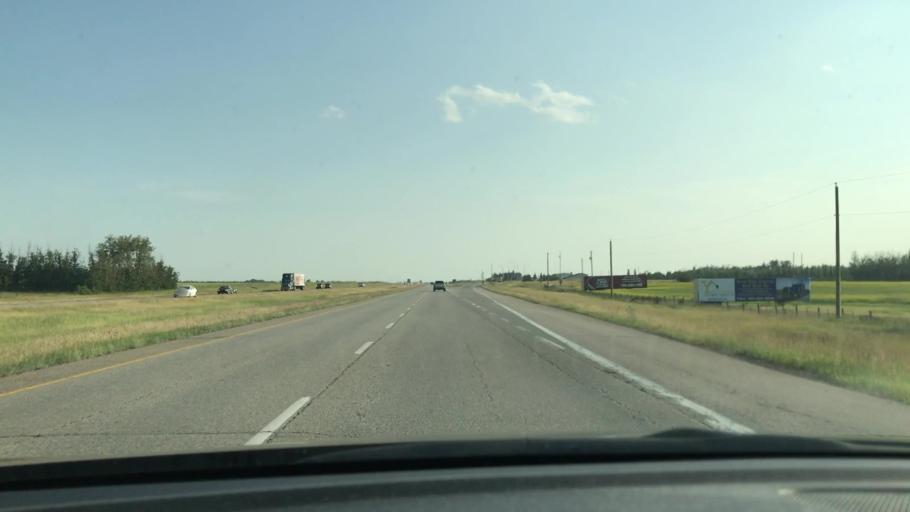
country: CA
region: Alberta
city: Leduc
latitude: 53.2378
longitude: -113.5663
